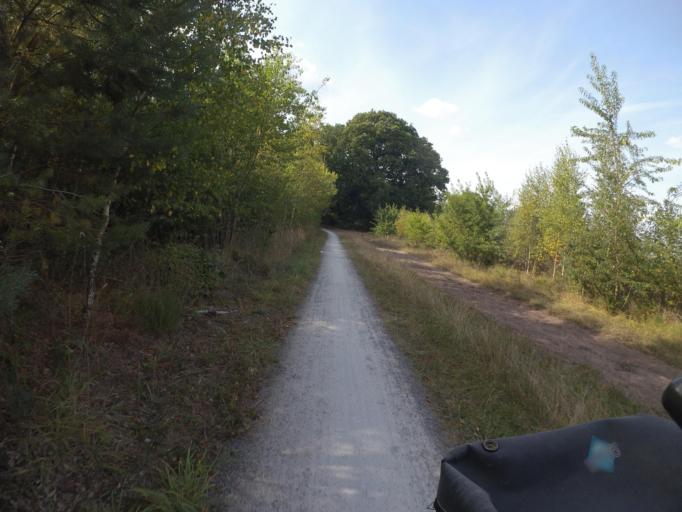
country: NL
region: Drenthe
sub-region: Gemeente Westerveld
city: Dwingeloo
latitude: 52.9220
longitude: 6.3279
